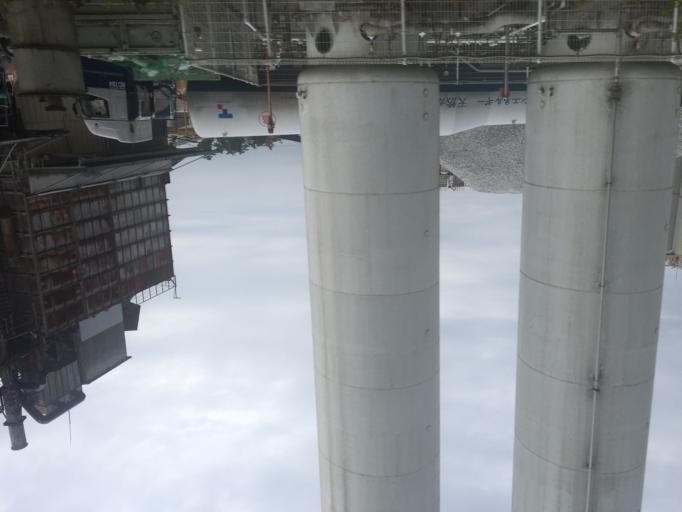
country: JP
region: Tokyo
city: Fussa
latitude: 35.7874
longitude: 139.3404
